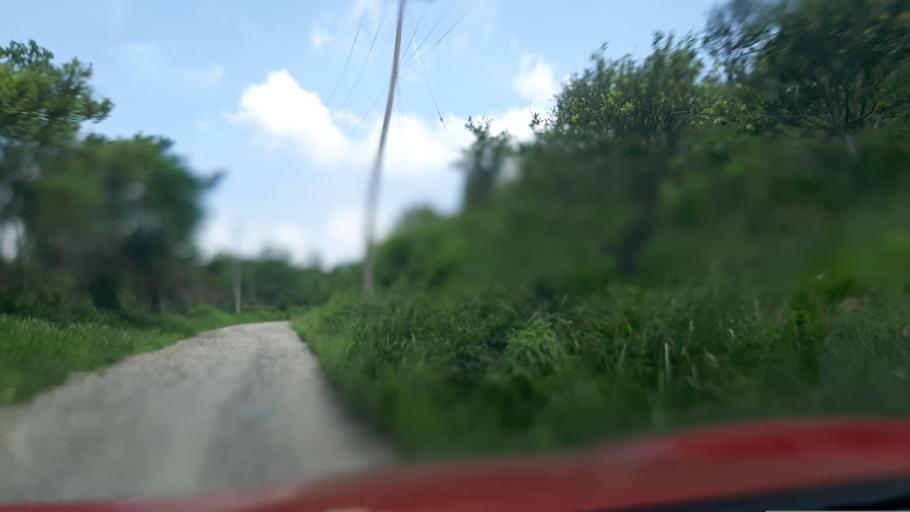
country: MX
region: Veracruz
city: Agua Dulce
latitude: 20.4152
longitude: -97.2787
